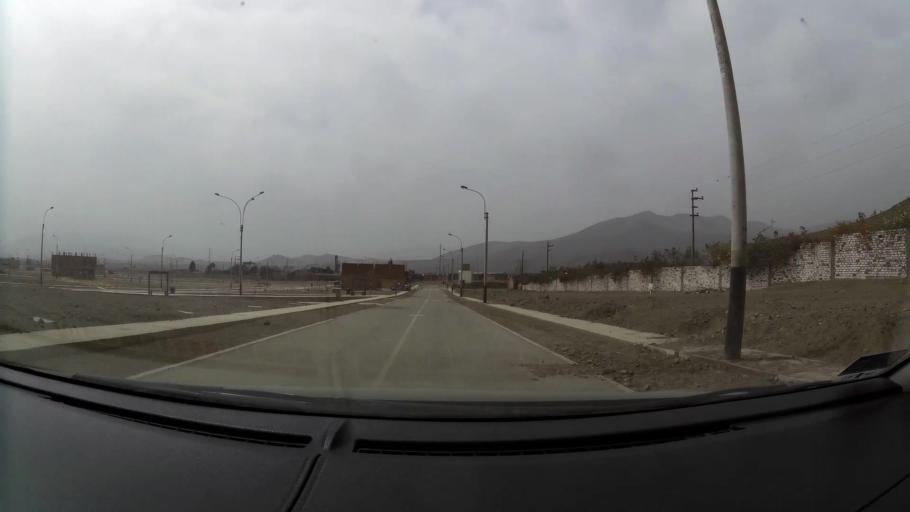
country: PE
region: Lima
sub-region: Lima
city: Santa Rosa
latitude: -11.7954
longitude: -77.1486
